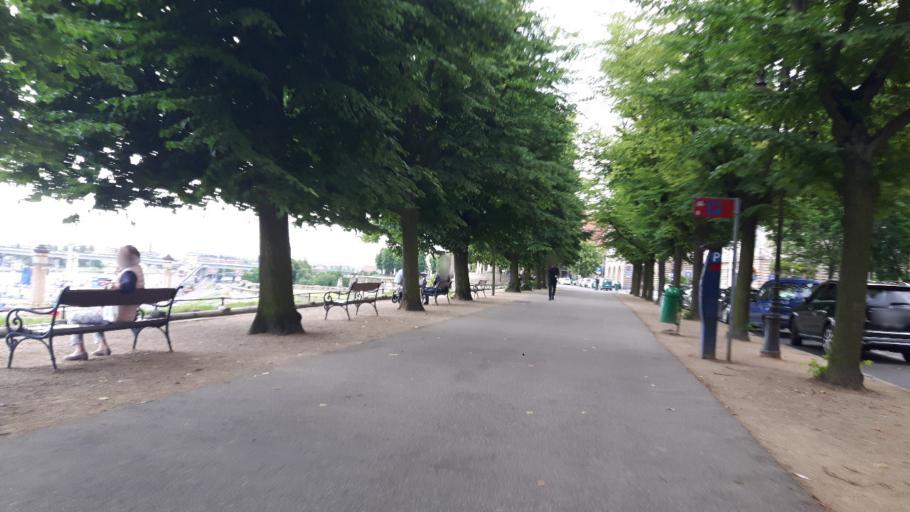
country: PL
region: West Pomeranian Voivodeship
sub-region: Szczecin
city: Szczecin
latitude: 53.4311
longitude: 14.5667
